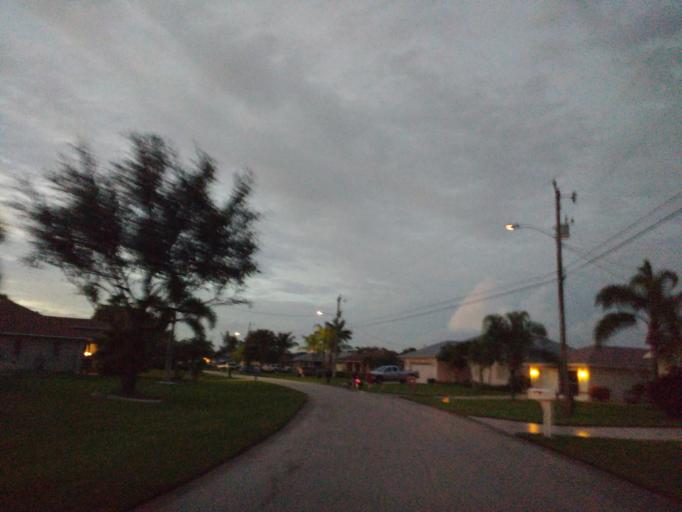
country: US
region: Florida
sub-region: Lee County
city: Cape Coral
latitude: 26.6156
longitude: -81.9631
